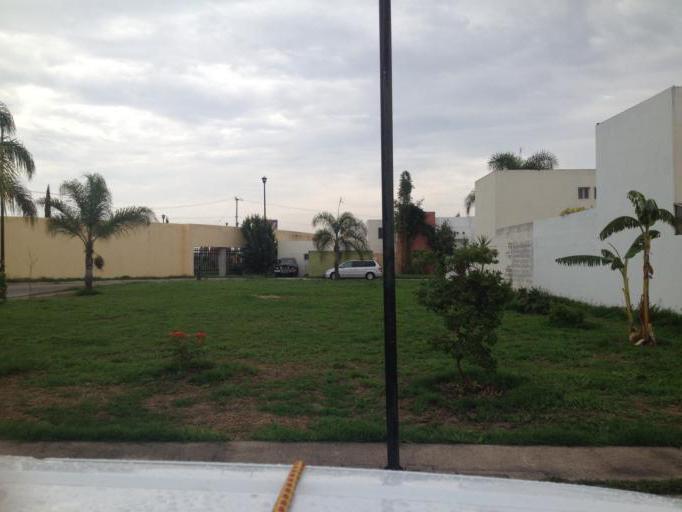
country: MX
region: Aguascalientes
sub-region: Aguascalientes
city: La Loma de los Negritos
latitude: 21.8441
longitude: -102.3294
